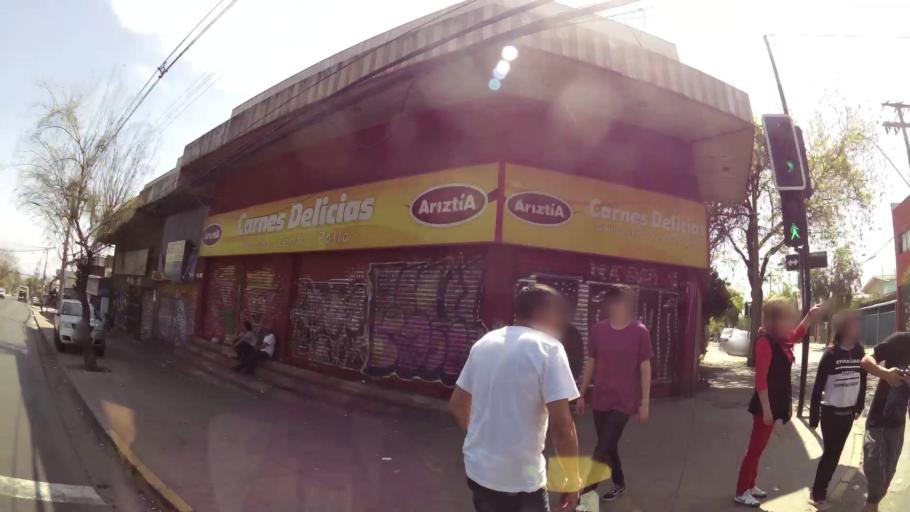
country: CL
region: Santiago Metropolitan
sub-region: Provincia de Santiago
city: Villa Presidente Frei, Nunoa, Santiago, Chile
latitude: -33.4722
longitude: -70.5388
